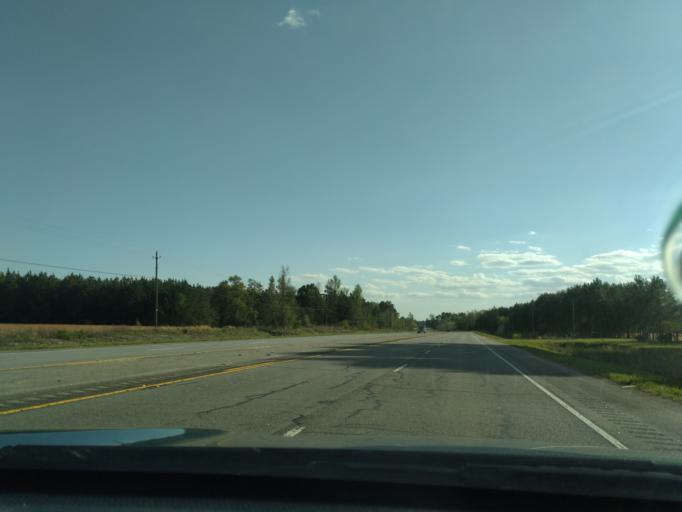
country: US
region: South Carolina
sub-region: Williamsburg County
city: Kingstree
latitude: 33.6279
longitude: -79.9233
